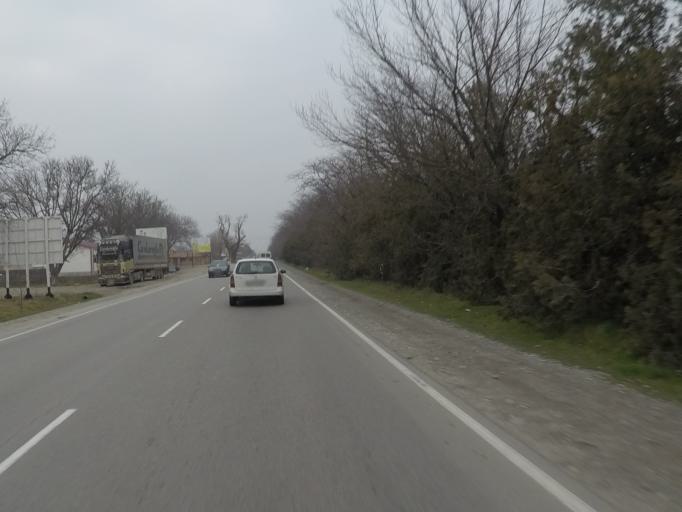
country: GE
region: Mtskheta-Mtianeti
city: Mtskheta
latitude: 41.9029
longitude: 44.7218
